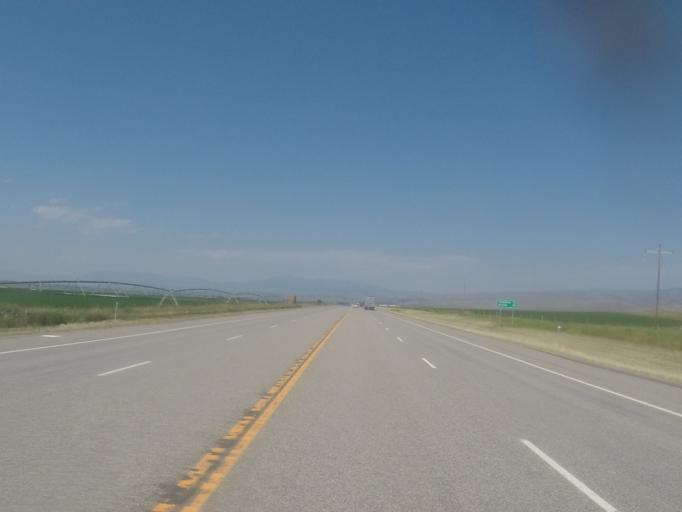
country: US
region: Montana
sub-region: Broadwater County
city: Townsend
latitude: 46.1111
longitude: -111.5070
